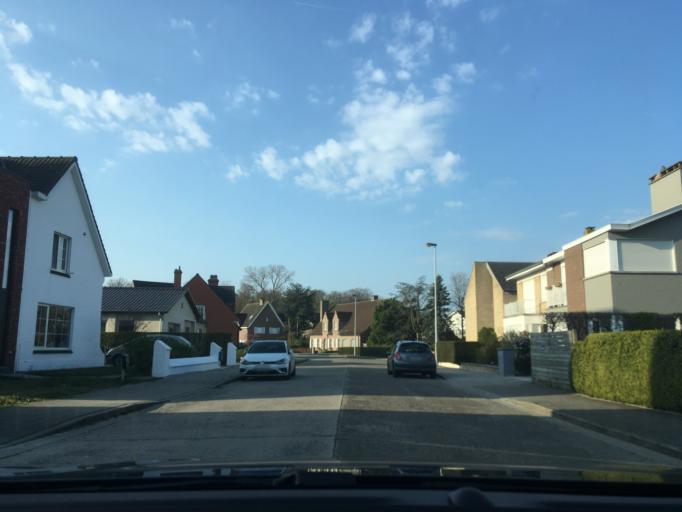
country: BE
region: Flanders
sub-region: Provincie West-Vlaanderen
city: Brugge
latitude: 51.1977
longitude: 3.2059
